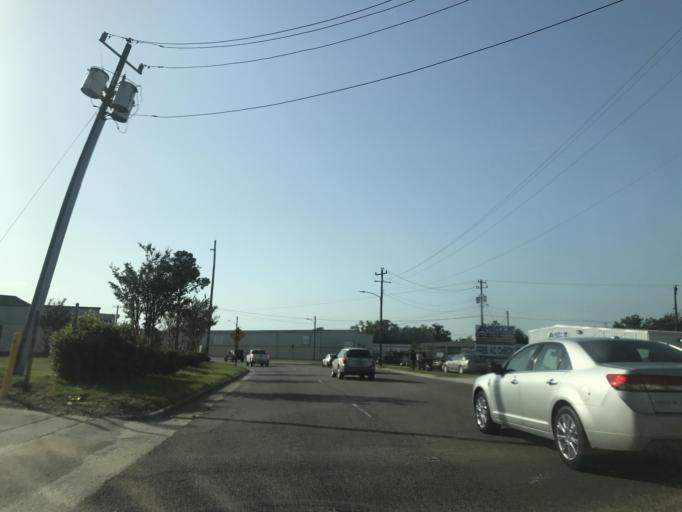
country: US
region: North Carolina
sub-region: New Hanover County
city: Wilmington
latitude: 34.2264
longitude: -77.9248
